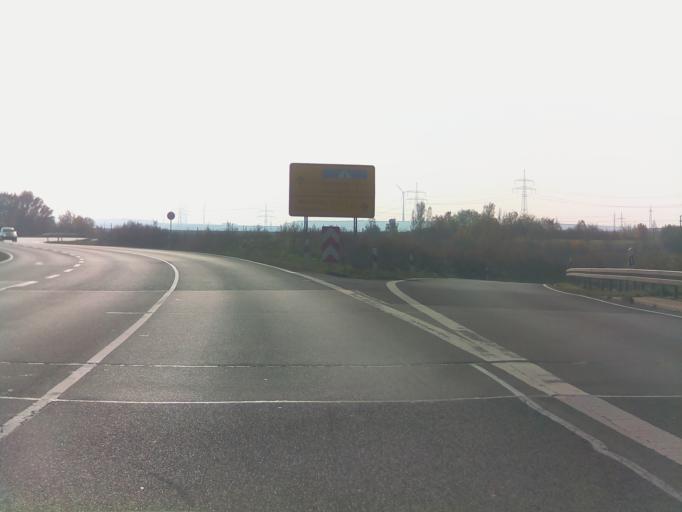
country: DE
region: Bavaria
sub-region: Regierungsbezirk Unterfranken
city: Biebelried
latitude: 49.7762
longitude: 10.0620
